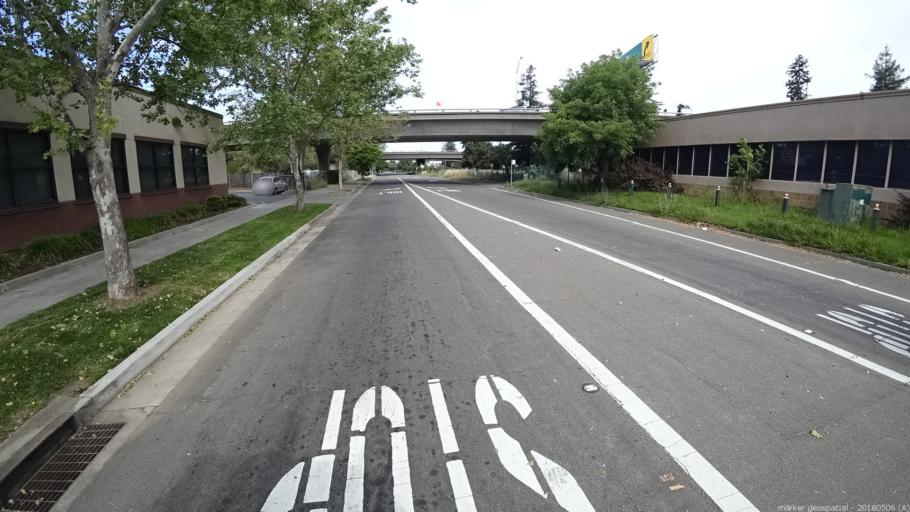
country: US
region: California
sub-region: Sacramento County
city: Sacramento
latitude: 38.5574
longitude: -121.4721
